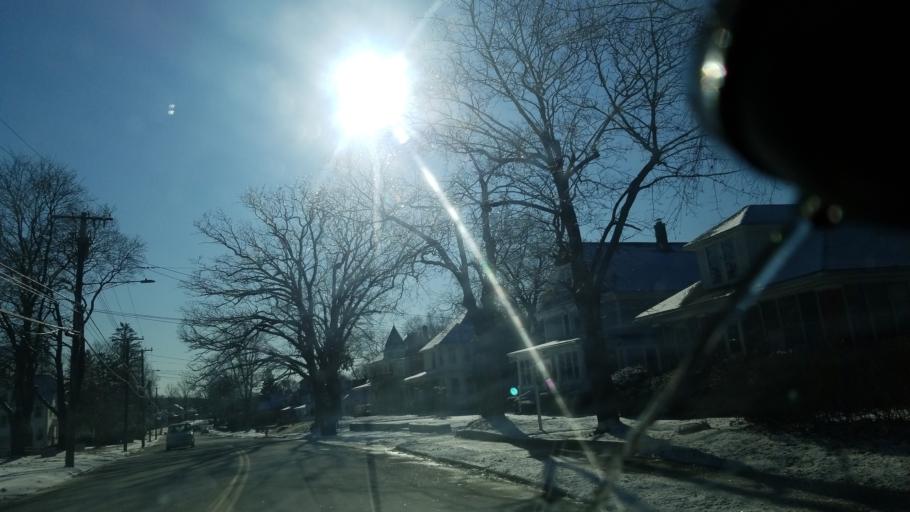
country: US
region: Connecticut
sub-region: Windham County
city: Danielson
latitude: 41.8016
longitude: -71.8804
